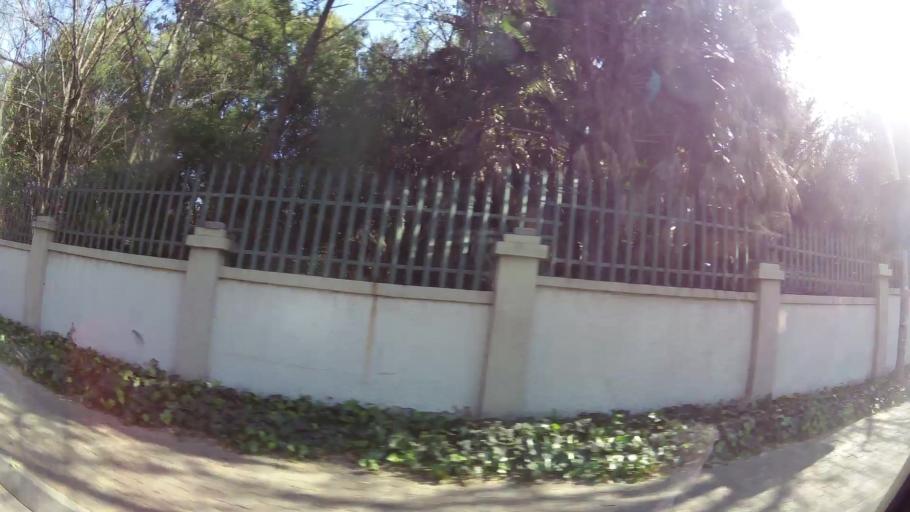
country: ZA
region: Gauteng
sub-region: City of Johannesburg Metropolitan Municipality
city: Johannesburg
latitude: -26.2627
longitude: 28.0586
